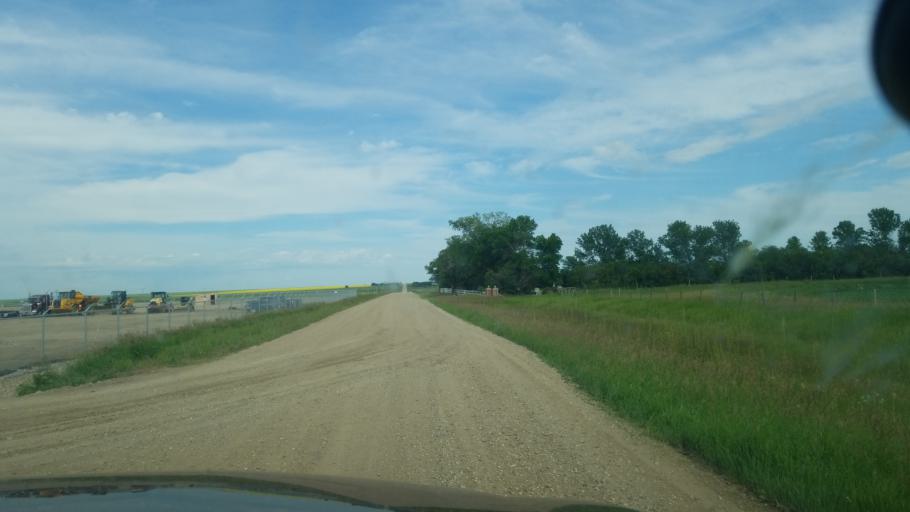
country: CA
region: Saskatchewan
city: Outlook
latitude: 51.4743
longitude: -107.5185
